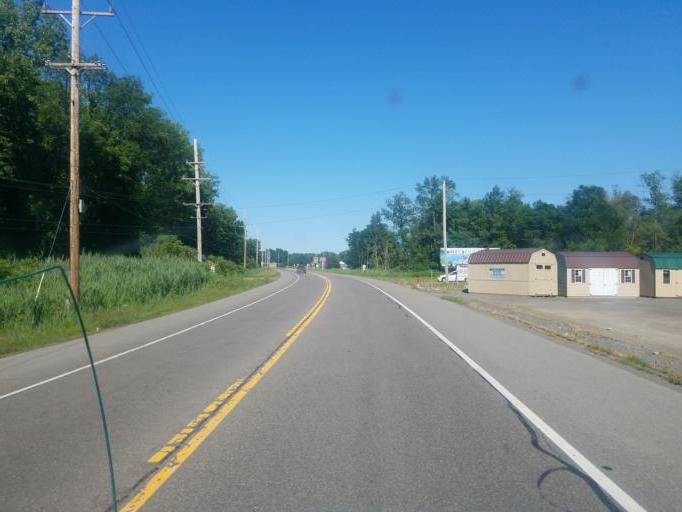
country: US
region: New York
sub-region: Wayne County
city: Lyons
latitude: 43.0590
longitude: -77.0069
